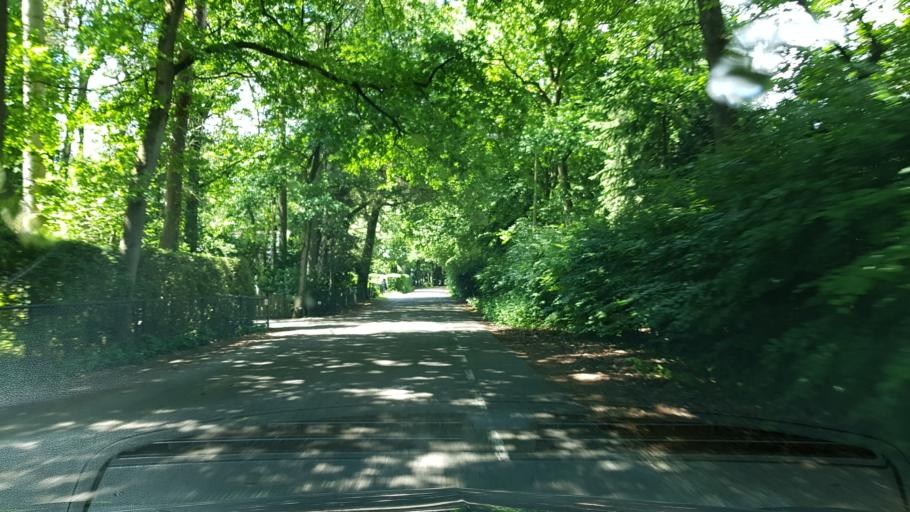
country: NL
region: Gelderland
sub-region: Gemeente Epe
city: Emst
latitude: 52.3444
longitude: 5.9350
